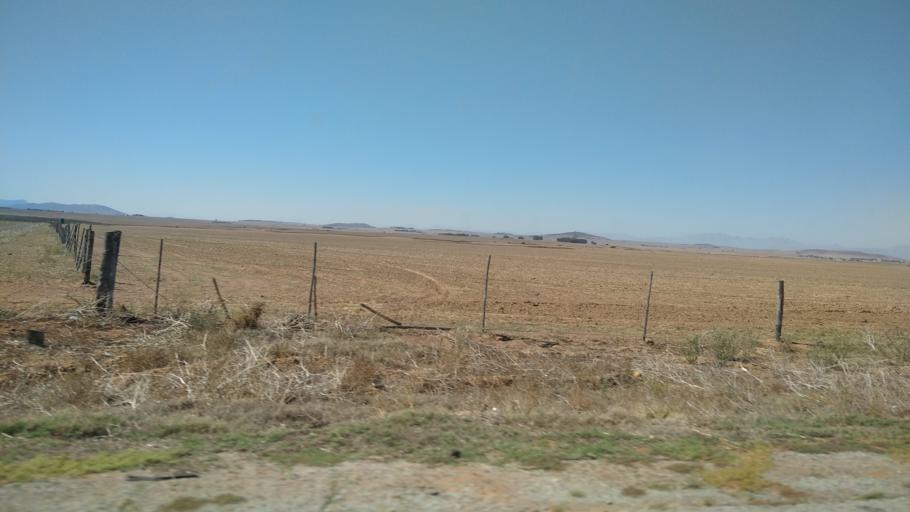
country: ZA
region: Western Cape
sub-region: West Coast District Municipality
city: Moorreesburg
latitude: -33.2294
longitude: 18.5560
